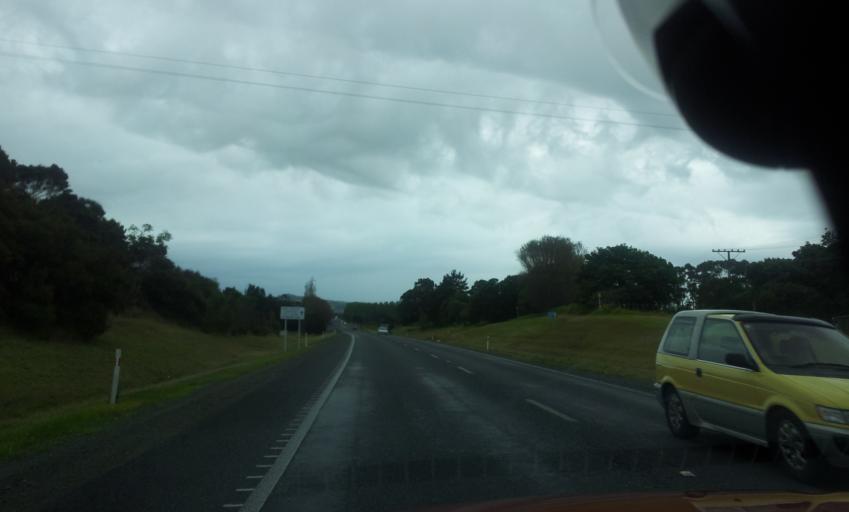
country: NZ
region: Northland
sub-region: Whangarei
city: Ruakaka
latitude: -35.9124
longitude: 174.4506
